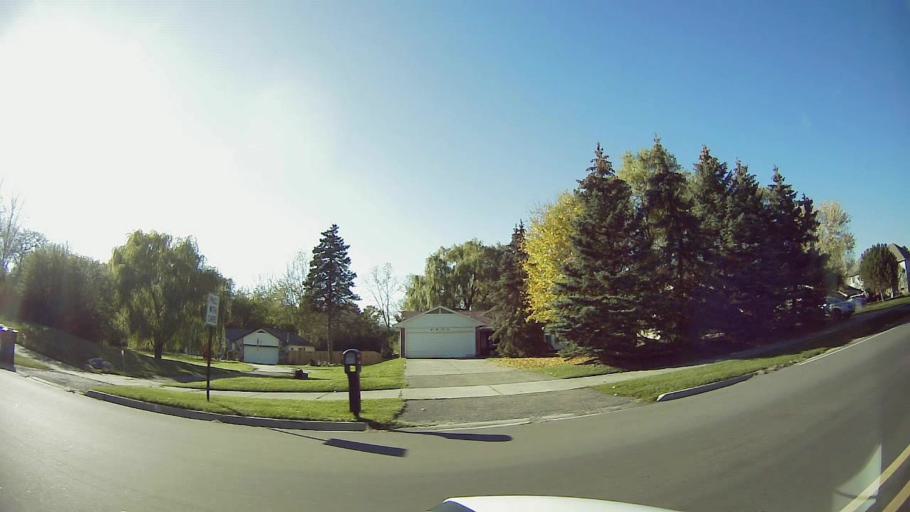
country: US
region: Michigan
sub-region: Oakland County
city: West Bloomfield Township
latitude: 42.5356
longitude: -83.3996
